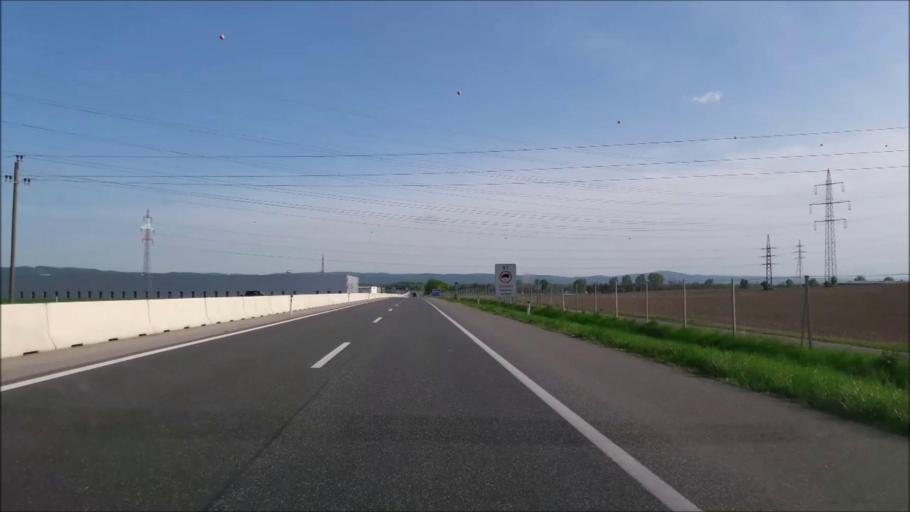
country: AT
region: Lower Austria
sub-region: Politischer Bezirk Korneuburg
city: Sierndorf
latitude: 48.3983
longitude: 16.1745
